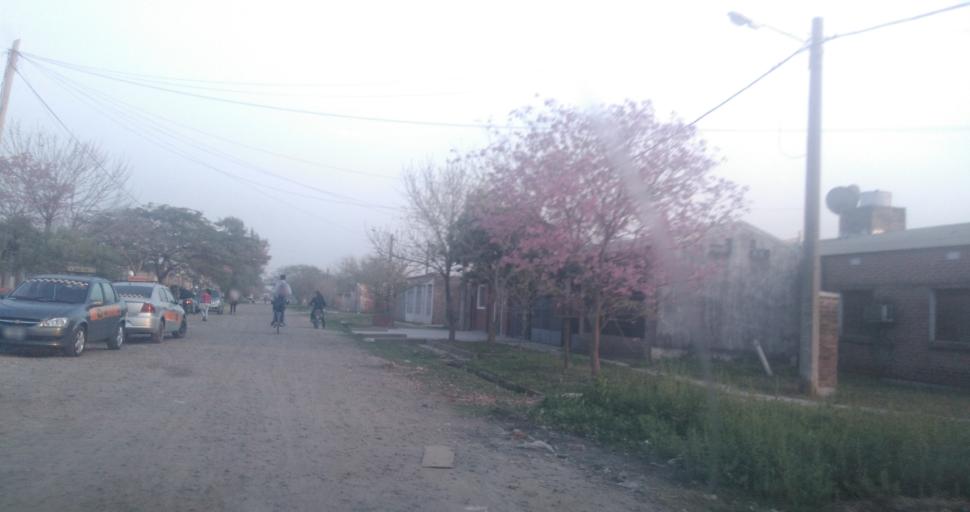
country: AR
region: Chaco
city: Resistencia
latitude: -27.4779
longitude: -59.0030
